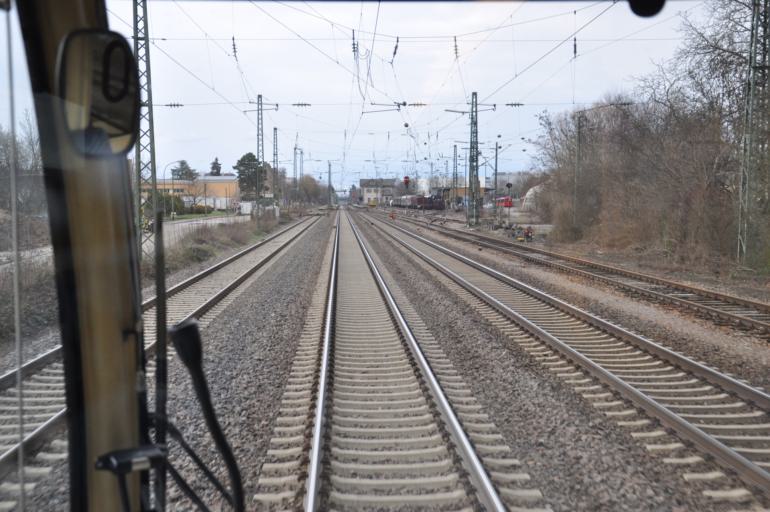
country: DE
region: Baden-Wuerttemberg
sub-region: Karlsruhe Region
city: Ettlingen
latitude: 48.9423
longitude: 8.3870
